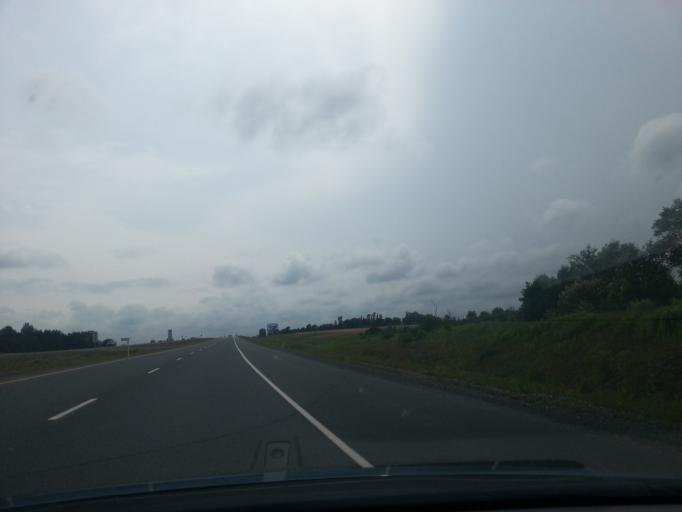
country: CA
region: New Brunswick
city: Florenceville-Bristol
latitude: 46.2065
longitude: -67.6028
